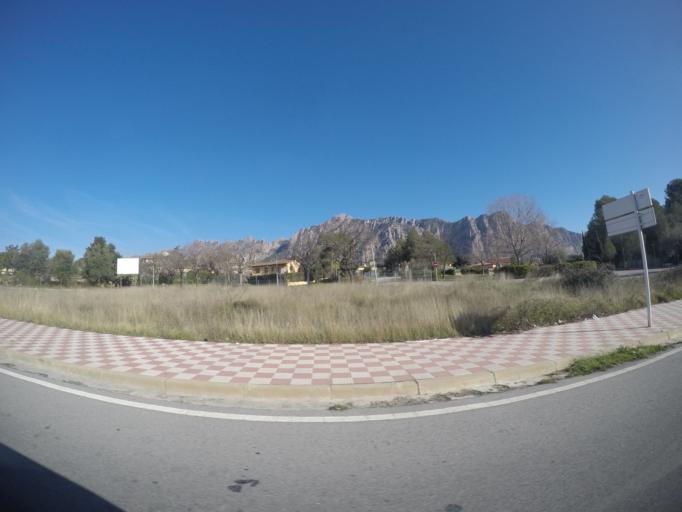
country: ES
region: Catalonia
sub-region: Provincia de Barcelona
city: Collbato
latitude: 41.5619
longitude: 1.8183
